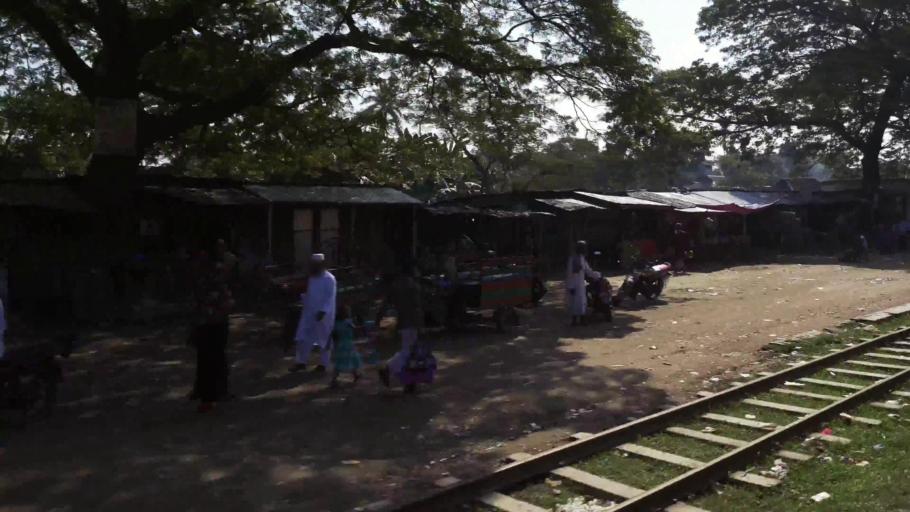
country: BD
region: Dhaka
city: Gafargaon
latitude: 24.4961
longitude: 90.5232
